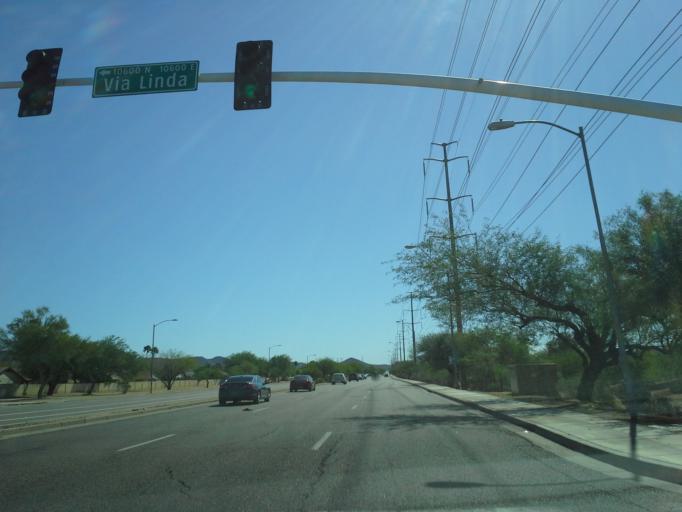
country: US
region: Arizona
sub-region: Maricopa County
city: Scottsdale
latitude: 33.5824
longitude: -111.8523
